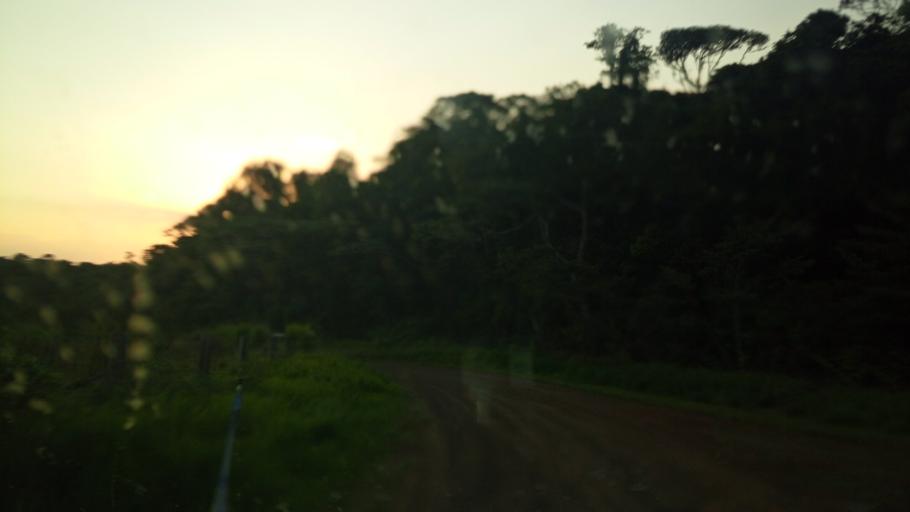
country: AU
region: Queensland
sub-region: Tablelands
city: Atherton
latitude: -17.3643
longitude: 145.7495
